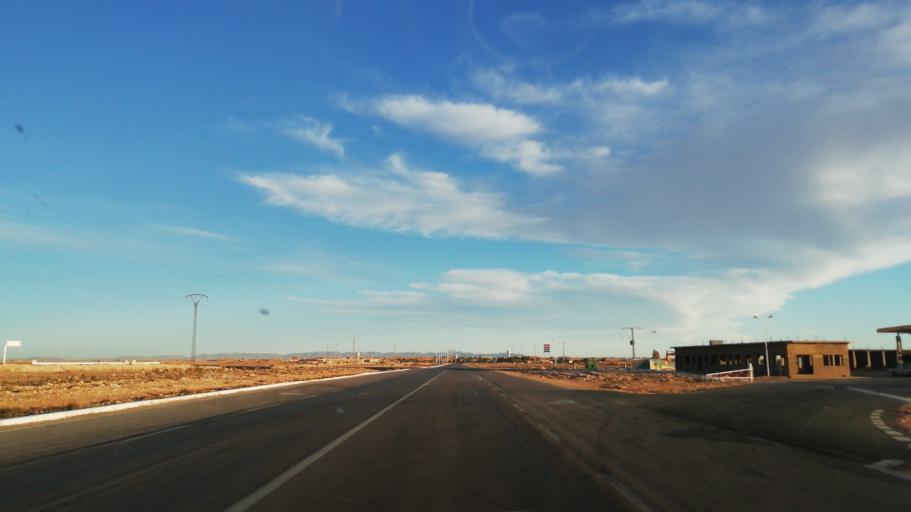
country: DZ
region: Wilaya de Naama
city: Naama
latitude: 33.7265
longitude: -0.7446
